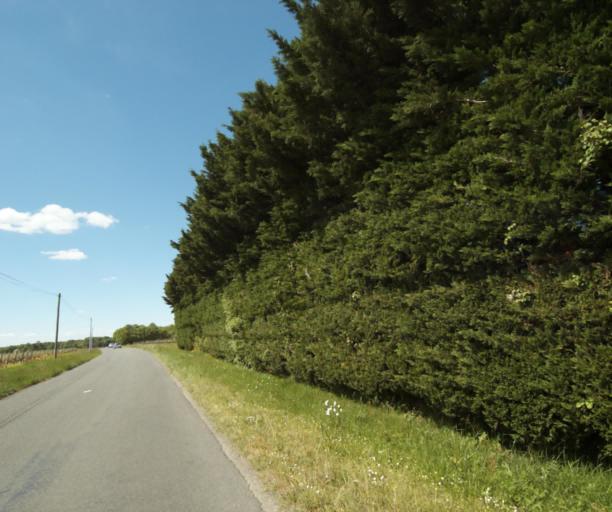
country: FR
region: Poitou-Charentes
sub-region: Departement de la Charente-Maritime
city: Burie
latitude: 45.7624
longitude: -0.4758
